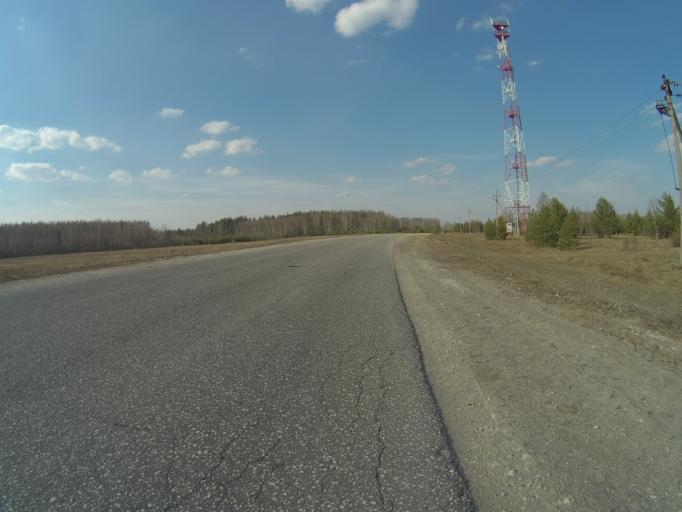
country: RU
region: Vladimir
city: Sudogda
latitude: 56.0995
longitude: 40.7823
